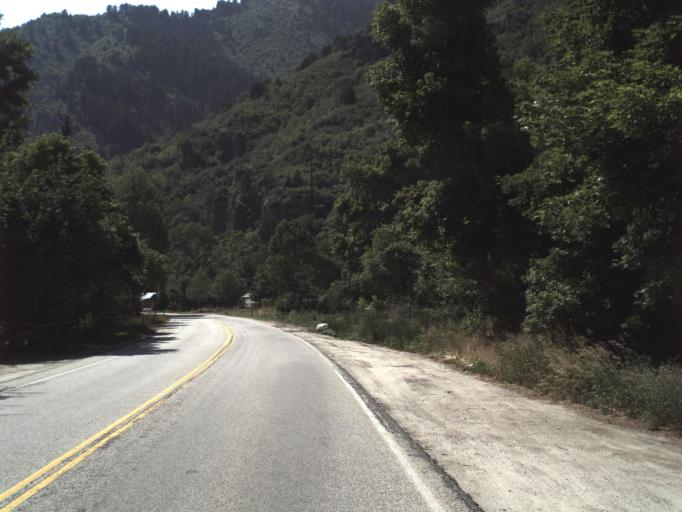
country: US
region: Utah
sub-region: Weber County
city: Liberty
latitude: 41.2551
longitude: -111.8699
